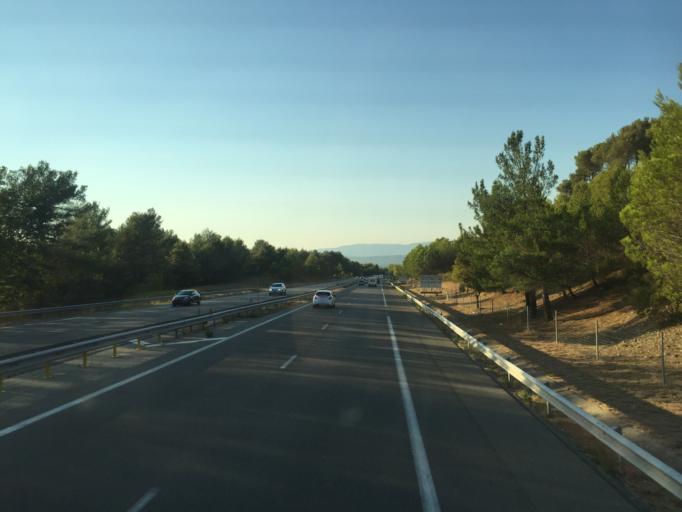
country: FR
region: Provence-Alpes-Cote d'Azur
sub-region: Departement des Bouches-du-Rhone
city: Venelles
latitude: 43.6186
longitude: 5.4947
